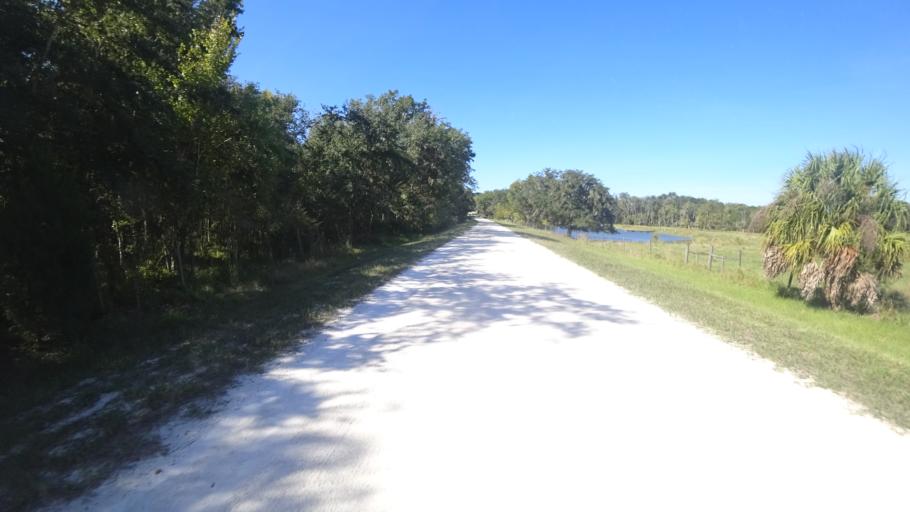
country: US
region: Florida
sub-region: Hillsborough County
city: Wimauma
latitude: 27.5963
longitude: -82.1921
